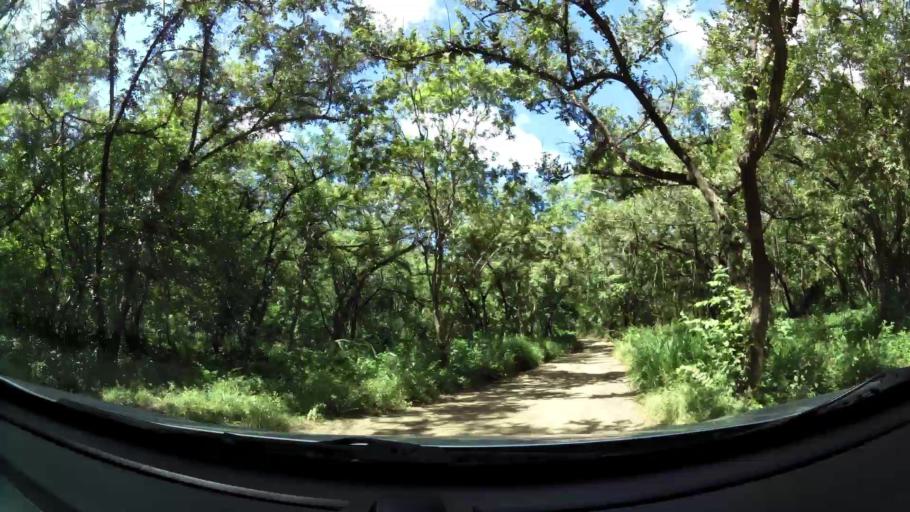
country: CR
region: Guanacaste
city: Bagaces
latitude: 10.5300
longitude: -85.2916
